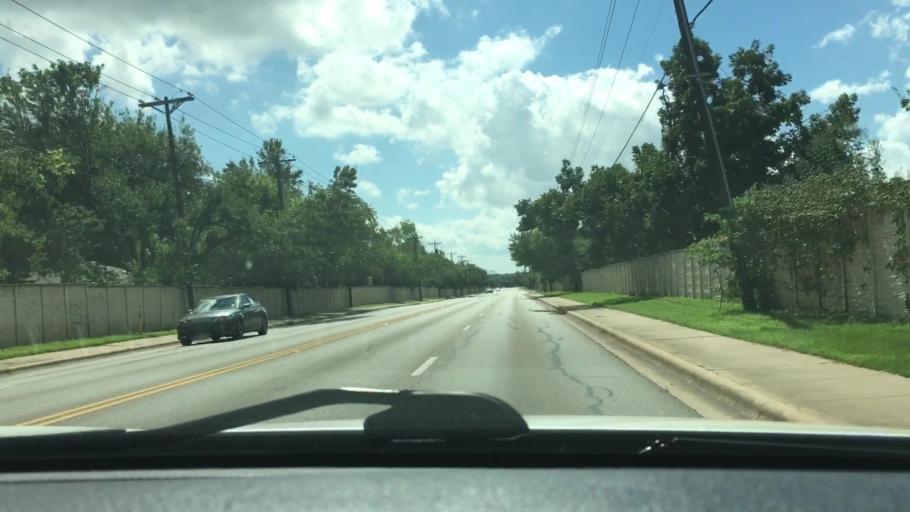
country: US
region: Texas
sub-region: Williamson County
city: Round Rock
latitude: 30.5247
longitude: -97.6679
